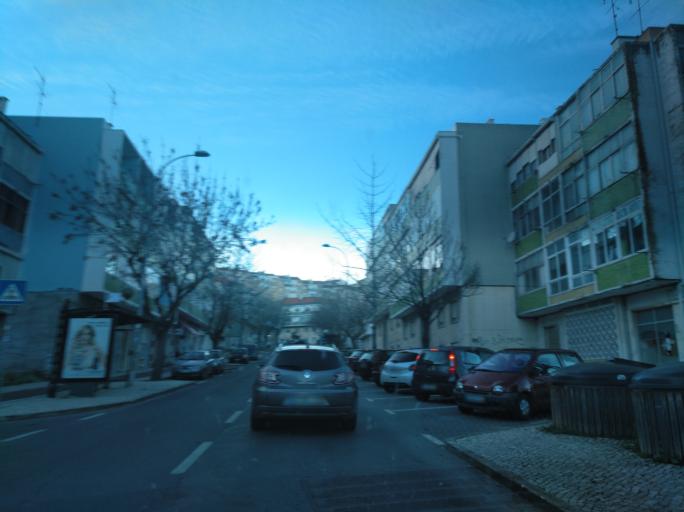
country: PT
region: Lisbon
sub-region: Amadora
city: Amadora
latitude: 38.7450
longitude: -9.2215
